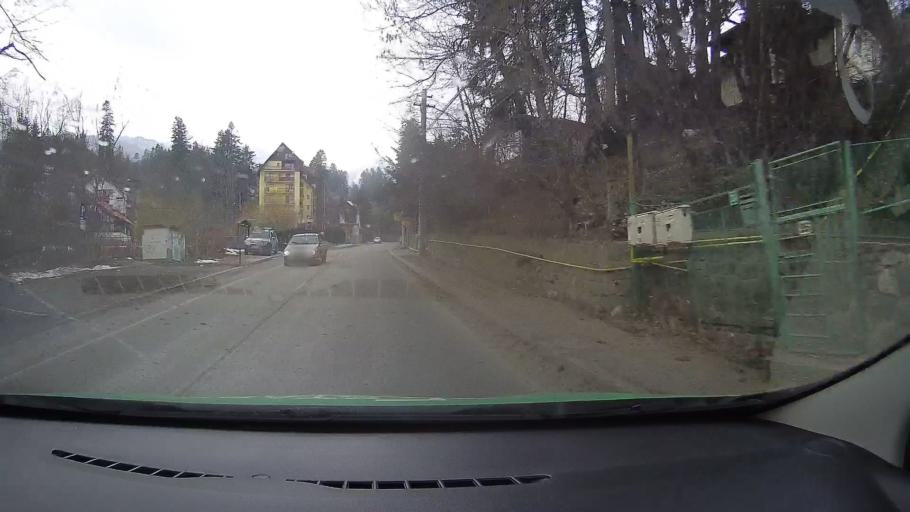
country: RO
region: Prahova
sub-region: Oras Sinaia
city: Sinaia
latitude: 45.3546
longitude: 25.5422
